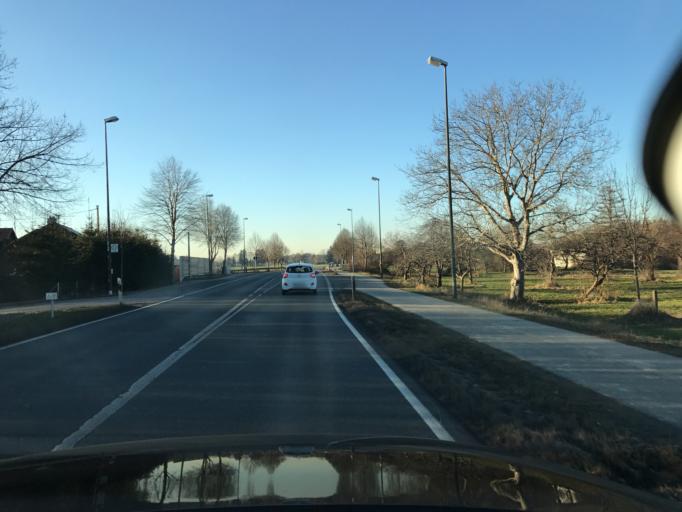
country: DE
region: Bavaria
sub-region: Upper Bavaria
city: Bad Aibling
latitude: 47.8440
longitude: 12.0270
